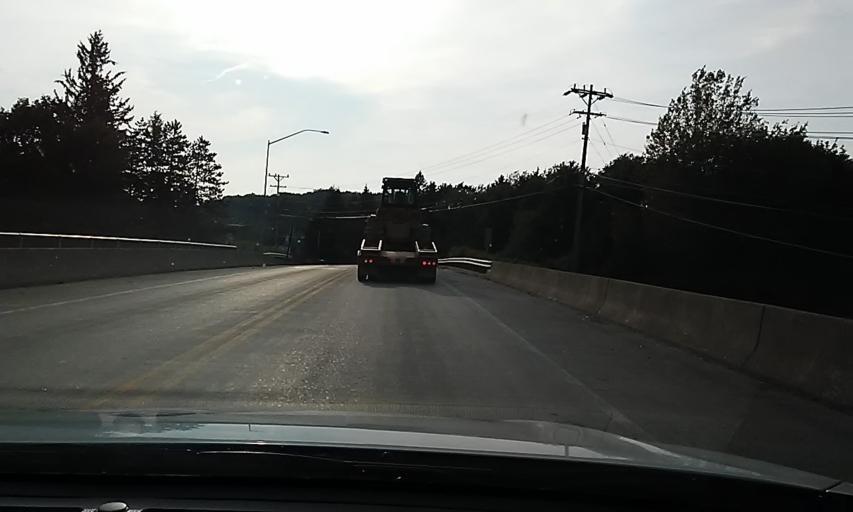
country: US
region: Pennsylvania
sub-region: McKean County
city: Kane
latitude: 41.7246
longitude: -78.6523
